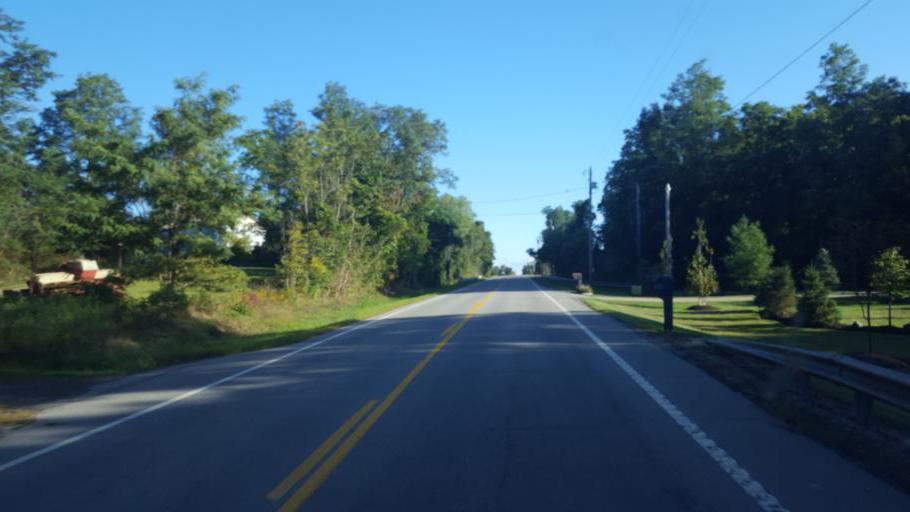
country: US
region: Ohio
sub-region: Lorain County
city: Camden
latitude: 41.1549
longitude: -82.3102
